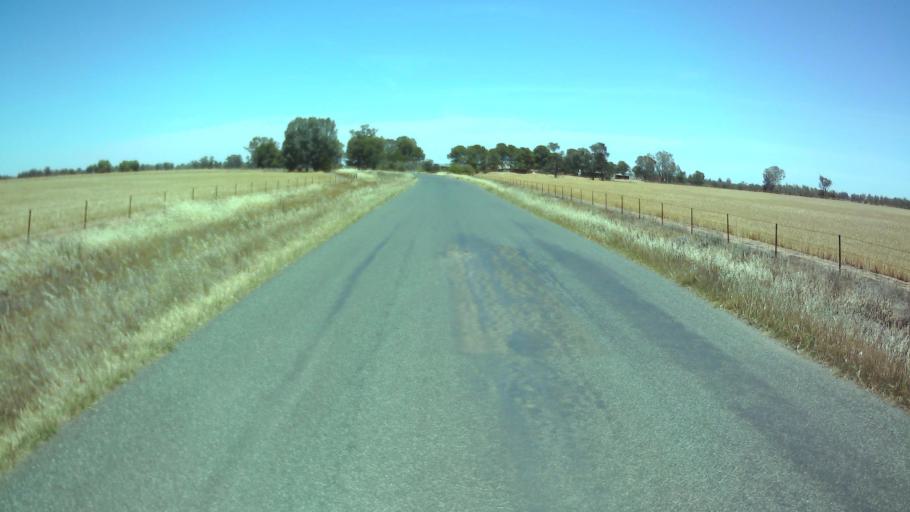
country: AU
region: New South Wales
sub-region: Weddin
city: Grenfell
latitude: -34.0443
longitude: 147.7849
